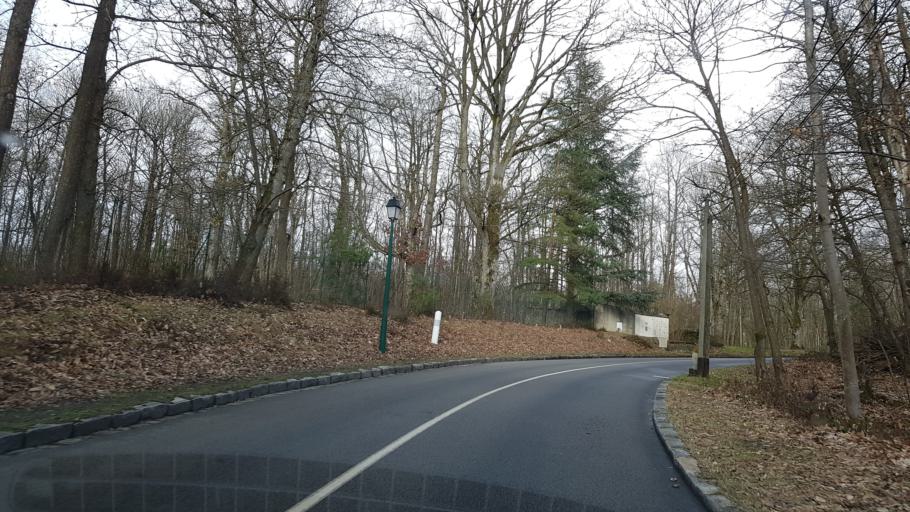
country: FR
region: Ile-de-France
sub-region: Departement des Yvelines
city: Saint-Arnoult-en-Yvelines
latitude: 48.6175
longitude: 1.9139
